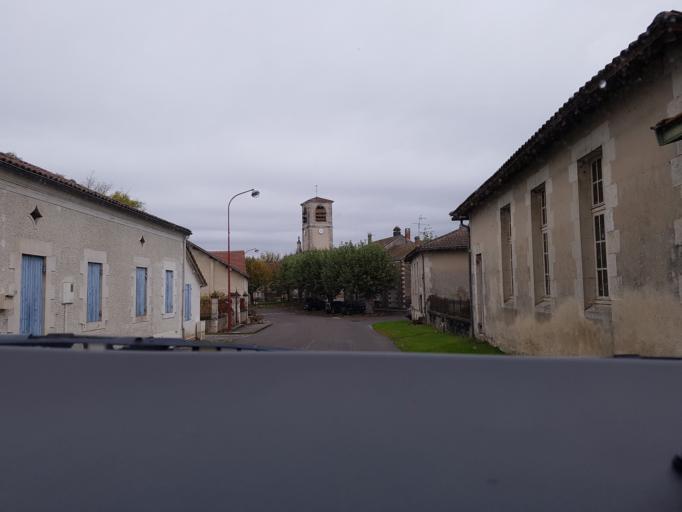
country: FR
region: Aquitaine
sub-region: Departement des Landes
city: Roquefort
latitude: 44.0992
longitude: -0.4061
